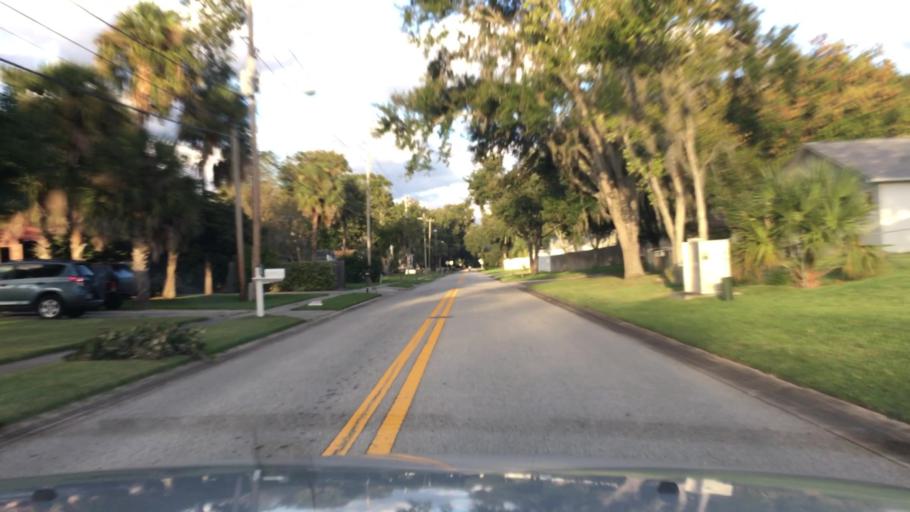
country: US
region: Florida
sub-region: Volusia County
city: Ormond Beach
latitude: 29.2625
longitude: -81.0690
